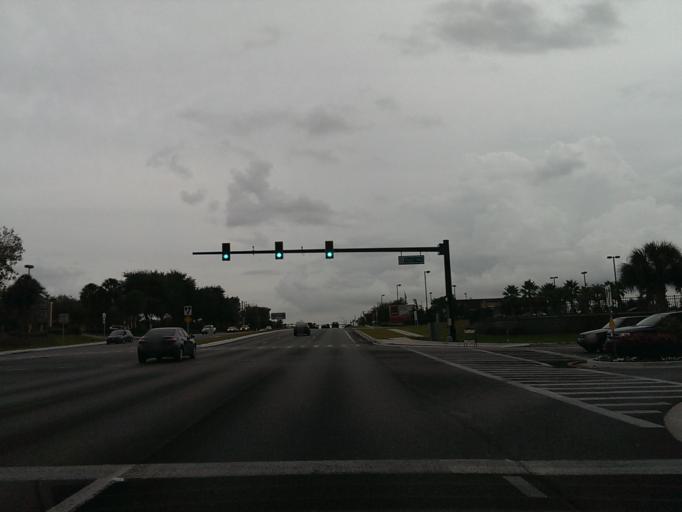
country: US
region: Florida
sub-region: Orange County
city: Gotha
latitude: 28.5518
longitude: -81.5096
